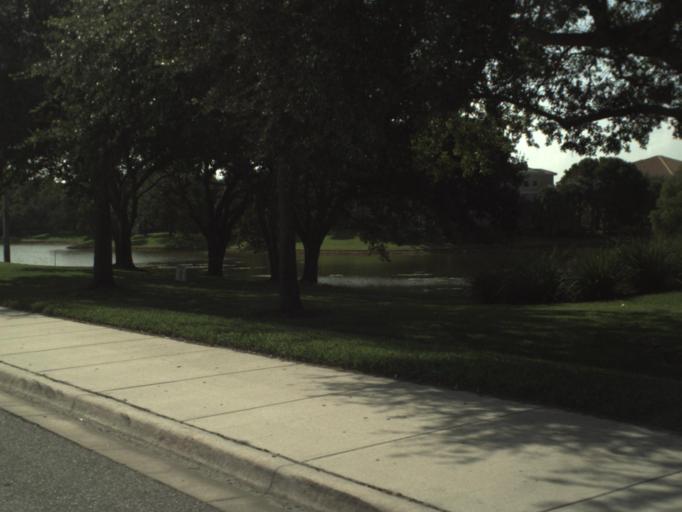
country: US
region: Florida
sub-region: Broward County
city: Margate
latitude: 26.2740
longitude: -80.2103
